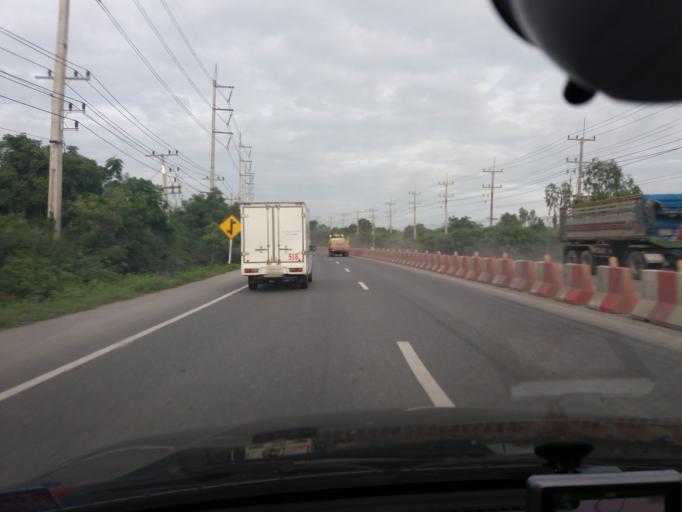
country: TH
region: Suphan Buri
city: U Thong
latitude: 14.3414
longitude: 99.8481
